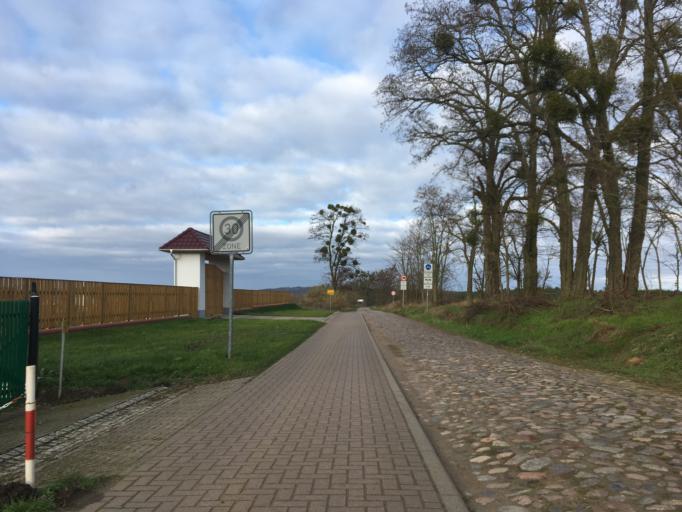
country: DE
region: Brandenburg
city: Muncheberg
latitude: 52.5587
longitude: 14.1374
